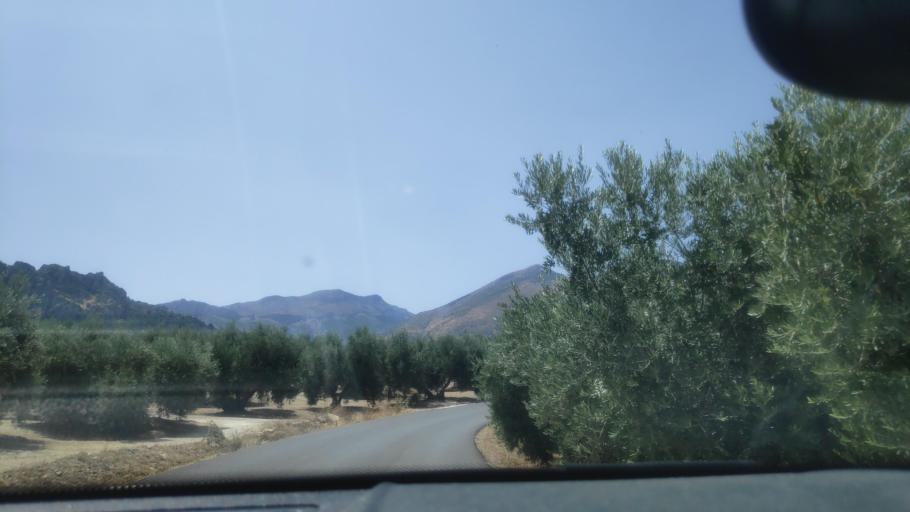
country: ES
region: Andalusia
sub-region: Provincia de Jaen
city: Jimena
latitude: 37.7997
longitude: -3.4461
